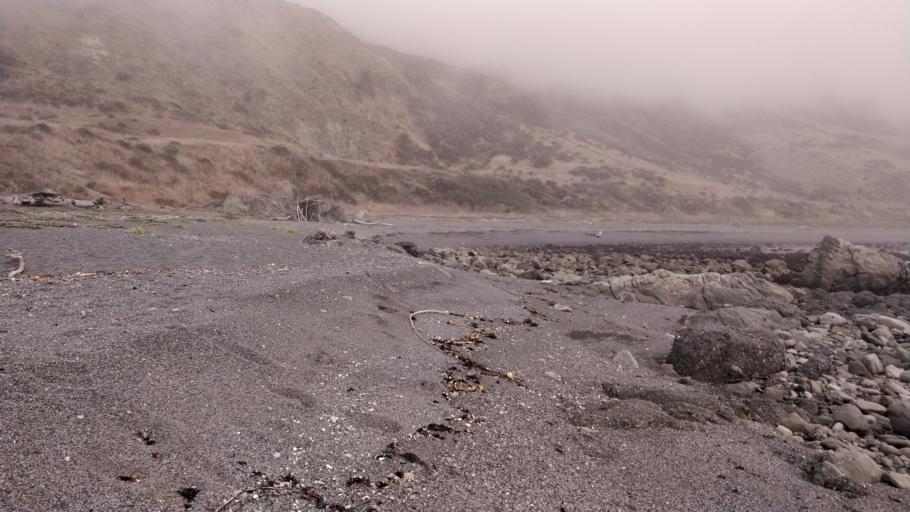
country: US
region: California
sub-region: Humboldt County
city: Ferndale
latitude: 40.4046
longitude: -124.3897
